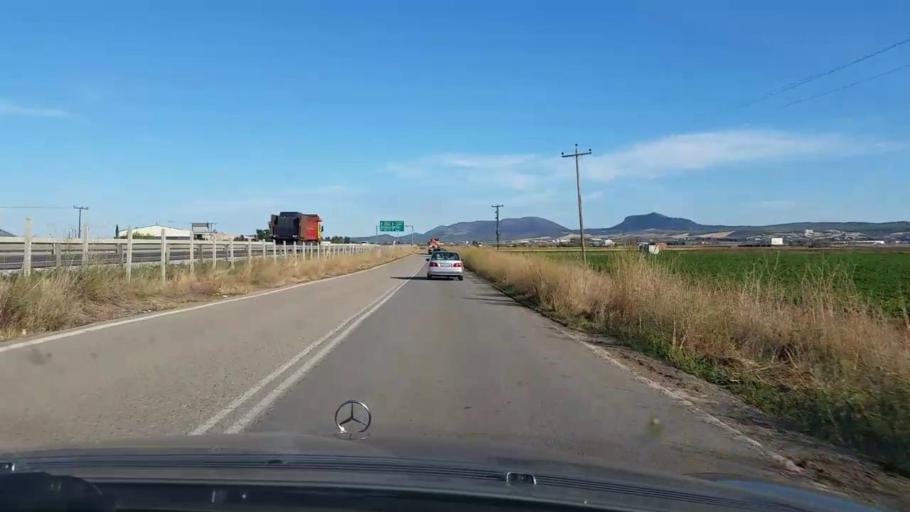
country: GR
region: Central Greece
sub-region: Nomos Voiotias
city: Thivai
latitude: 38.3653
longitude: 23.3098
